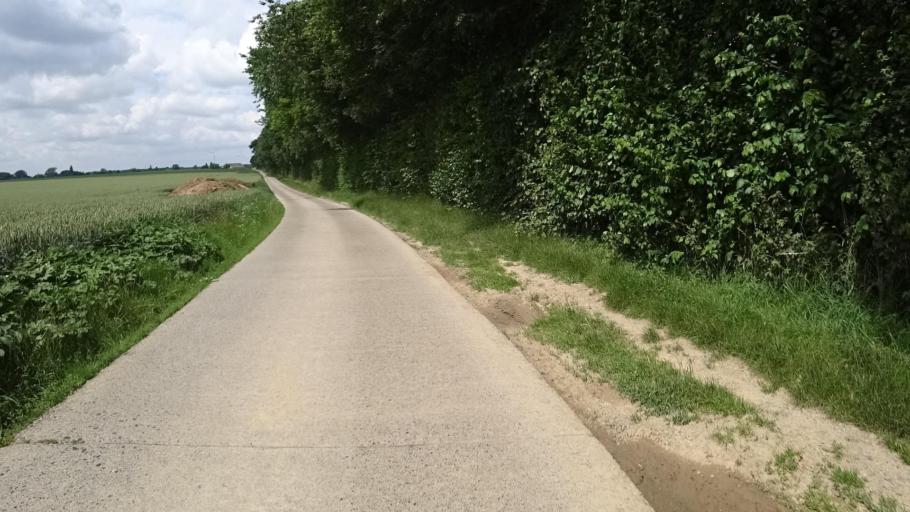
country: BE
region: Wallonia
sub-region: Province du Brabant Wallon
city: Perwez
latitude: 50.5682
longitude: 4.8246
